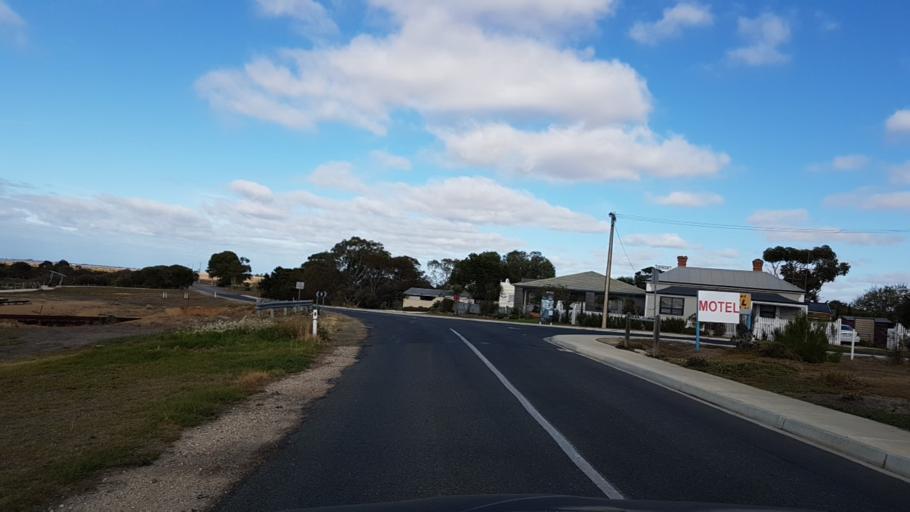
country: AU
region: South Australia
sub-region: Alexandrina
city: Langhorne Creek
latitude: -35.4098
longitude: 138.9705
